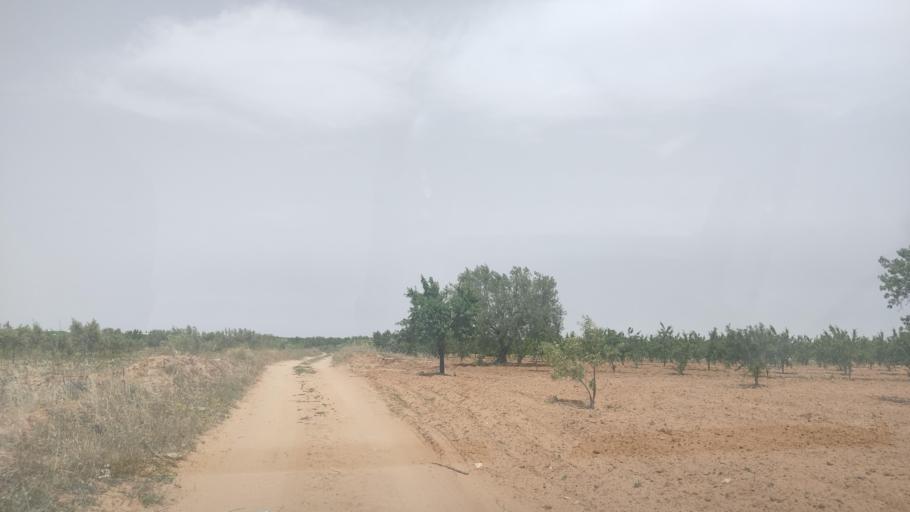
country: TN
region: Safaqis
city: Sfax
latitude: 34.8427
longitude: 10.5923
